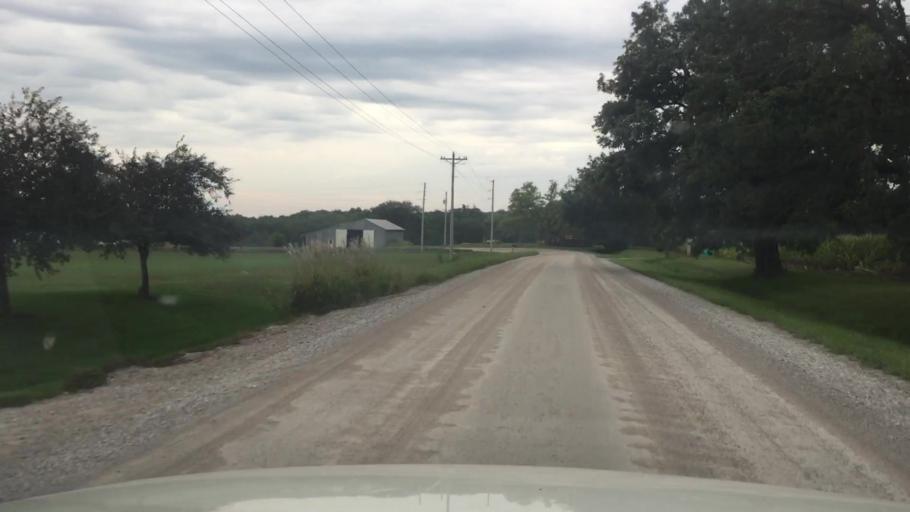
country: US
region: Iowa
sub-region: Story County
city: Huxley
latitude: 41.9129
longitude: -93.5766
